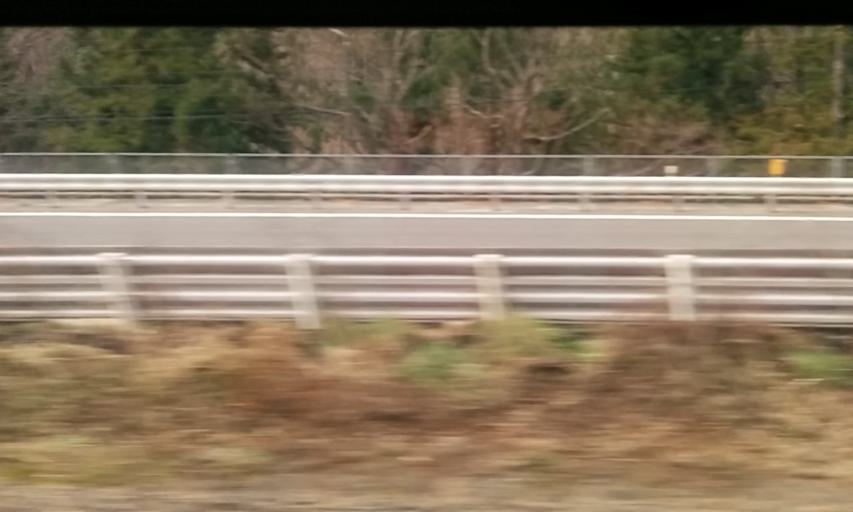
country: JP
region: Nagano
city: Shiojiri
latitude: 36.0445
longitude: 137.8912
